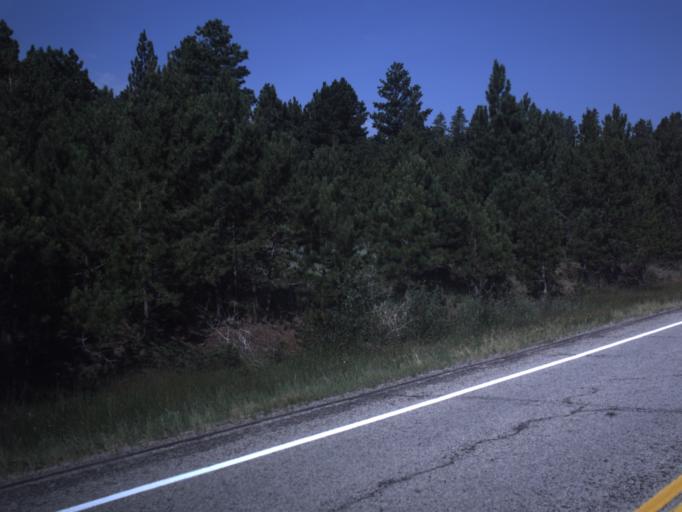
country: US
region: Utah
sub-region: Daggett County
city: Manila
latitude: 40.8509
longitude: -109.5887
